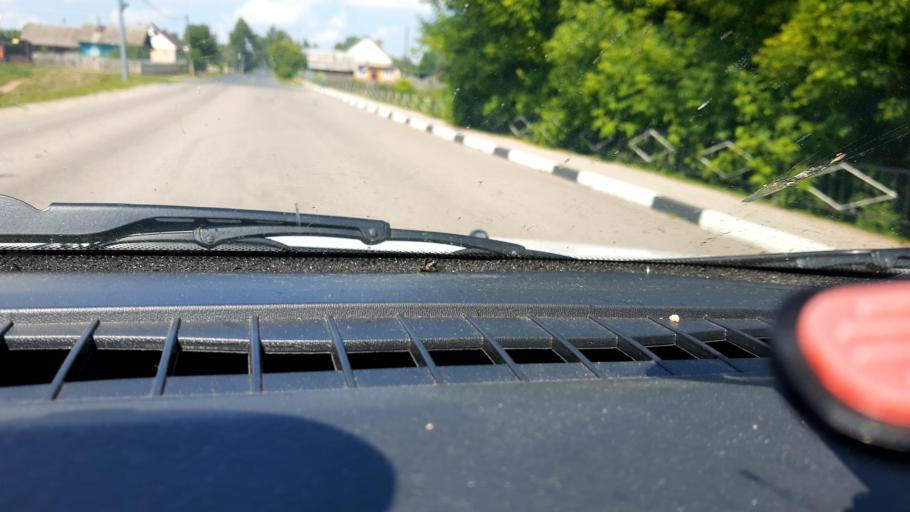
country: RU
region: Nizjnij Novgorod
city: Sharanga
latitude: 57.1699
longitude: 46.5413
